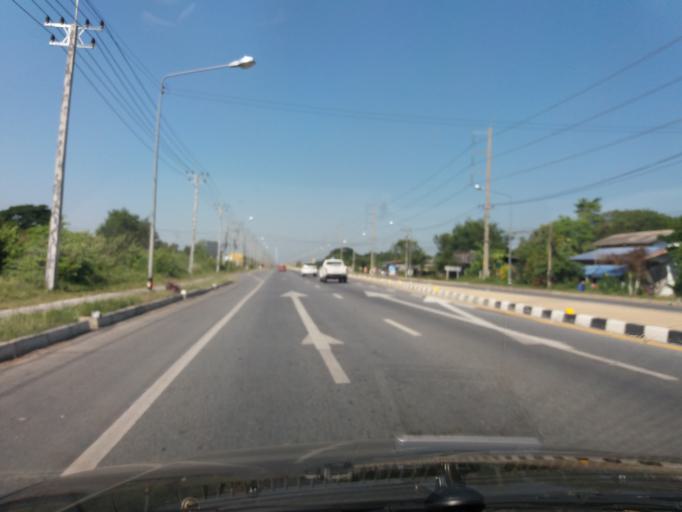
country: TH
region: Chai Nat
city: Manorom
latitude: 15.2691
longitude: 100.0934
